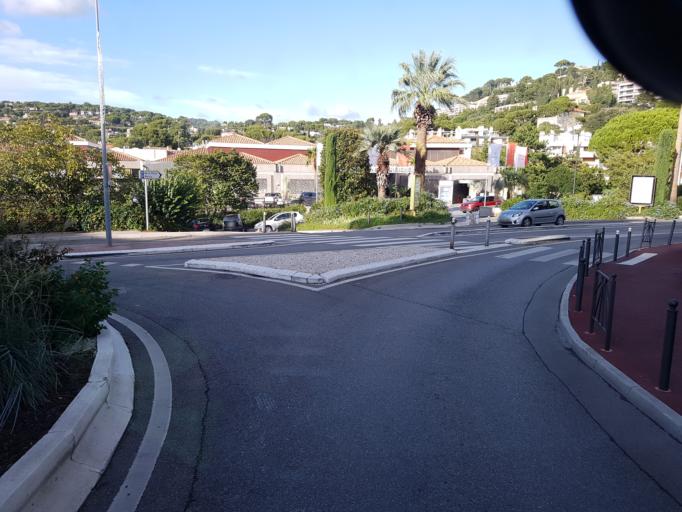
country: FR
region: Provence-Alpes-Cote d'Azur
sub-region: Departement des Bouches-du-Rhone
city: Cassis
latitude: 43.2137
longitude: 5.5418
